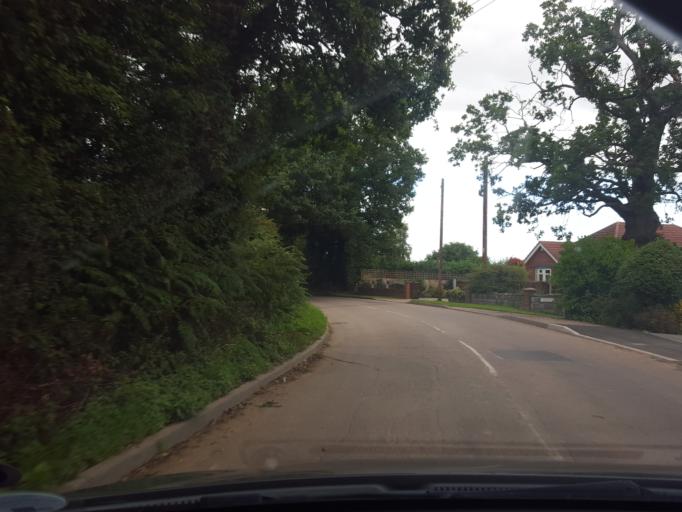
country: GB
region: England
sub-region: Essex
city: Great Bentley
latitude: 51.8462
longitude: 1.0375
